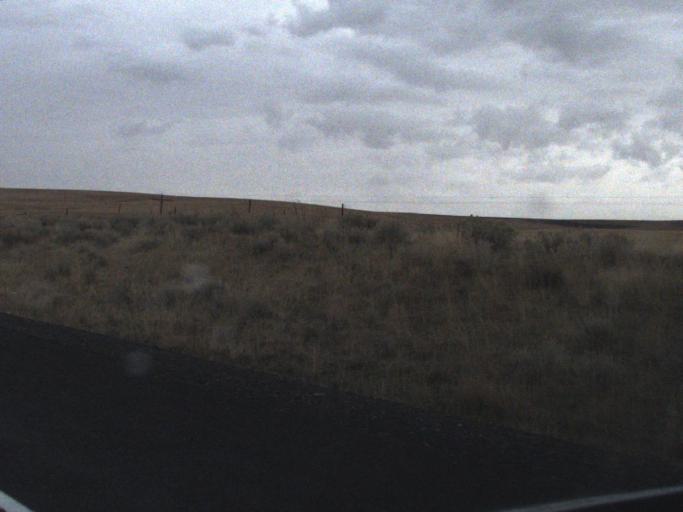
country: US
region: Washington
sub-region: Columbia County
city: Dayton
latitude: 46.7623
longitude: -117.9891
